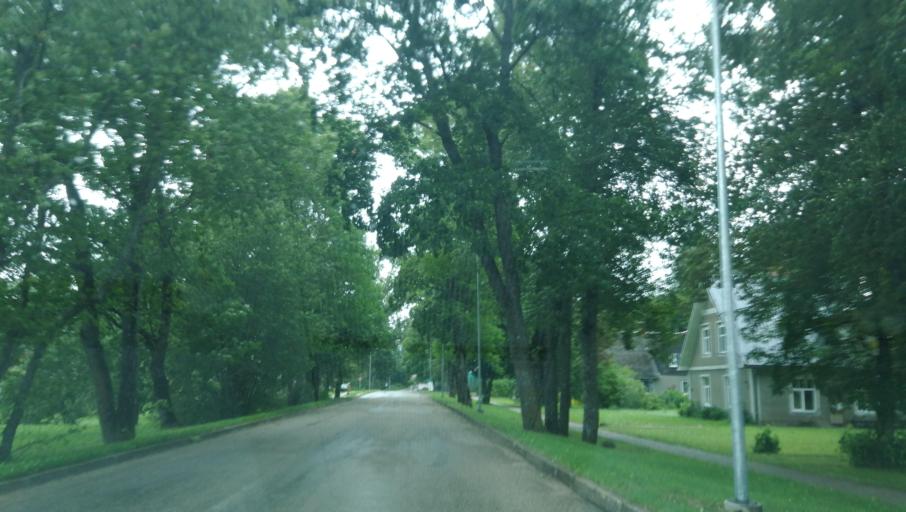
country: LV
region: Beverina
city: Murmuiza
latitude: 57.4739
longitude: 25.4910
